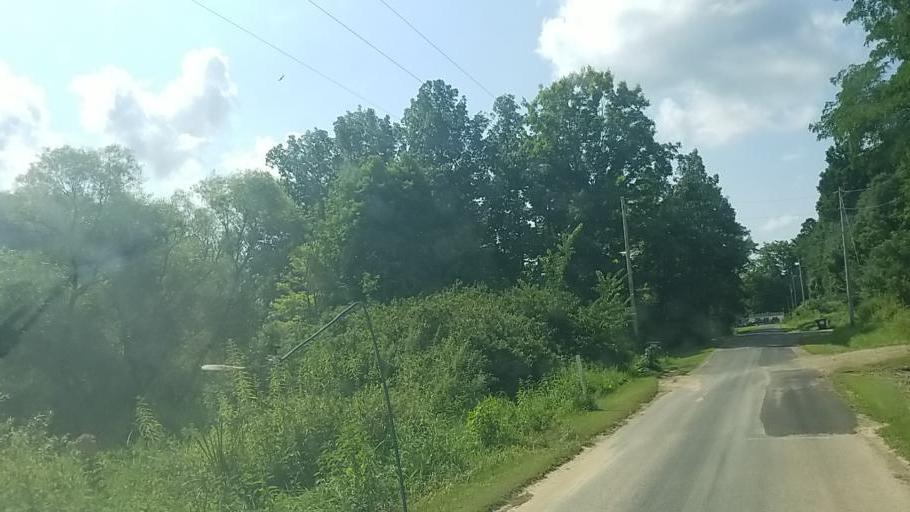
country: US
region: Ohio
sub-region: Ashland County
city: Ashland
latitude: 40.7501
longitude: -82.3000
